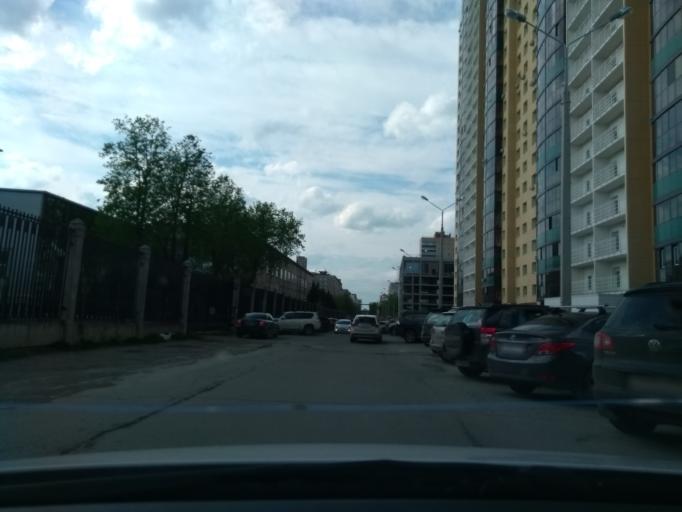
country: RU
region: Perm
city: Perm
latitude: 58.0003
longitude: 56.2669
